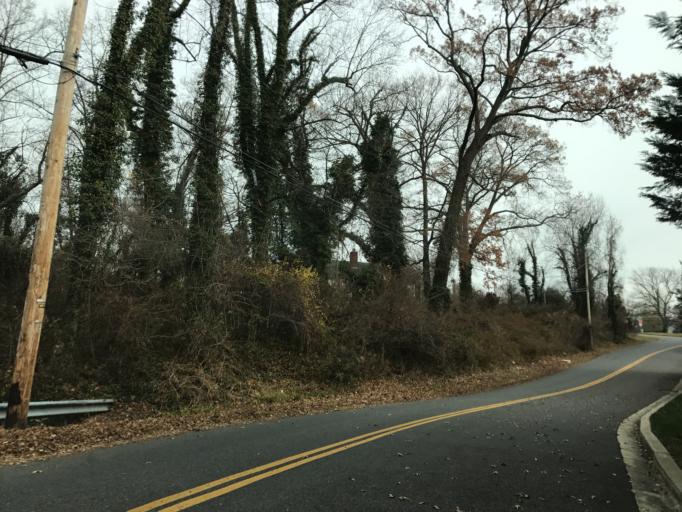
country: US
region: Maryland
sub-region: Anne Arundel County
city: Arnold
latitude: 39.0310
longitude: -76.5051
